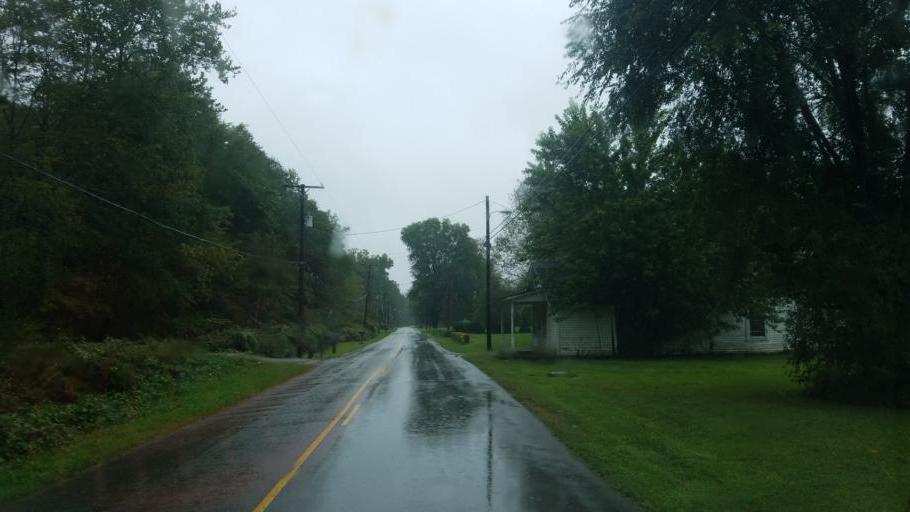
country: US
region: Ohio
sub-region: Scioto County
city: West Portsmouth
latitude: 38.7323
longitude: -83.0604
